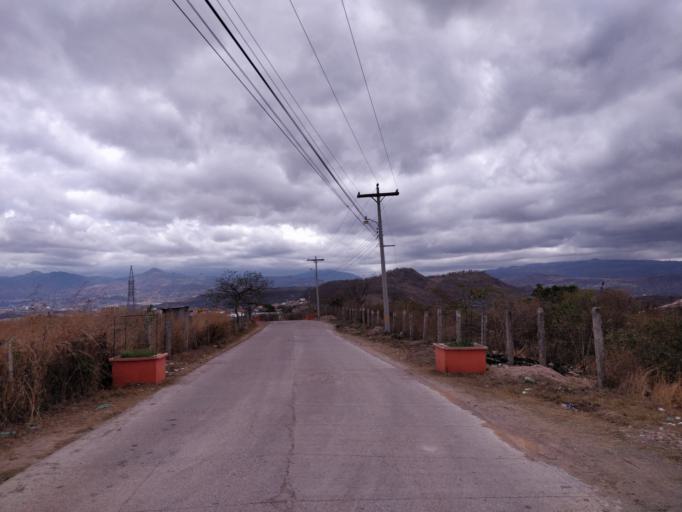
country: HN
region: Francisco Morazan
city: Yaguacire
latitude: 14.0342
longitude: -87.2451
